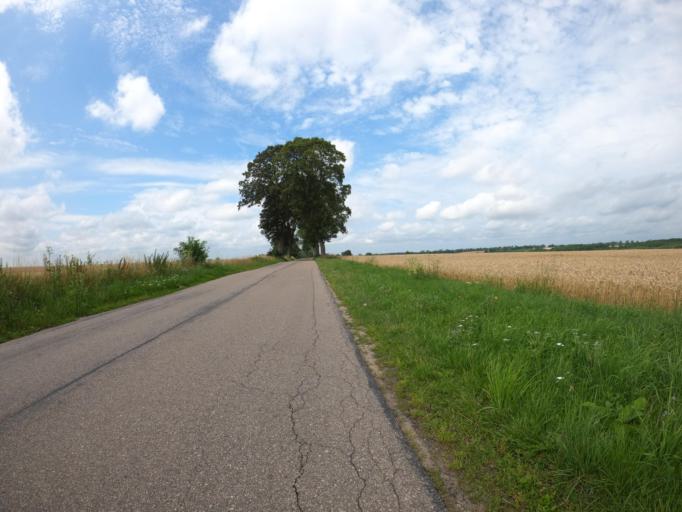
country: PL
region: West Pomeranian Voivodeship
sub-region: Powiat szczecinecki
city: Grzmiaca
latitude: 53.7904
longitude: 16.4812
